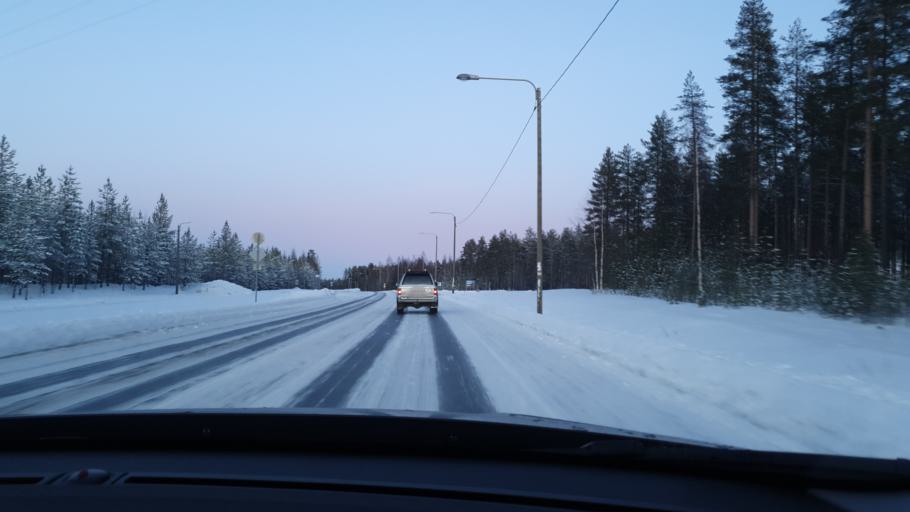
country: FI
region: Kainuu
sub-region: Kehys-Kainuu
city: Kuhmo
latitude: 64.0982
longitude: 29.4724
